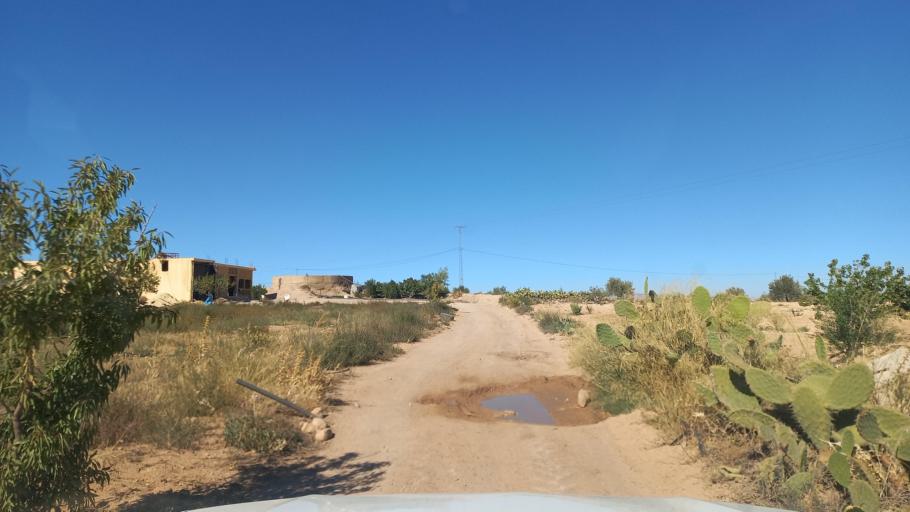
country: TN
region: Al Qasrayn
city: Sbiba
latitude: 35.3982
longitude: 9.0843
